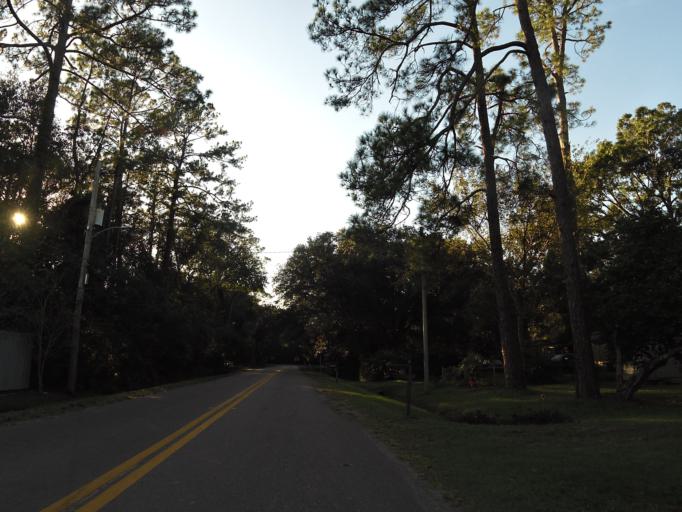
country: US
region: Florida
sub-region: Duval County
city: Jacksonville
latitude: 30.3612
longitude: -81.7627
